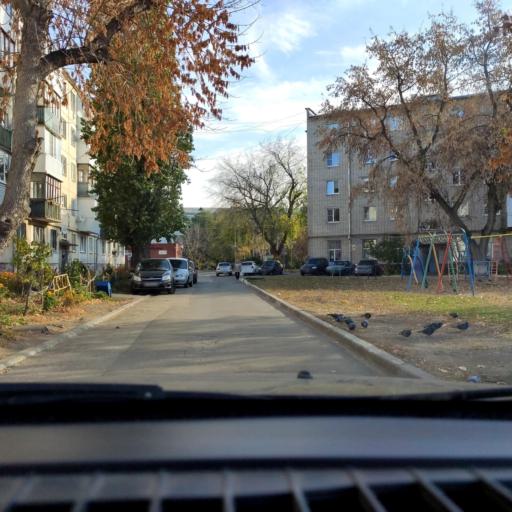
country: RU
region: Samara
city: Tol'yatti
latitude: 53.5314
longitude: 49.4238
